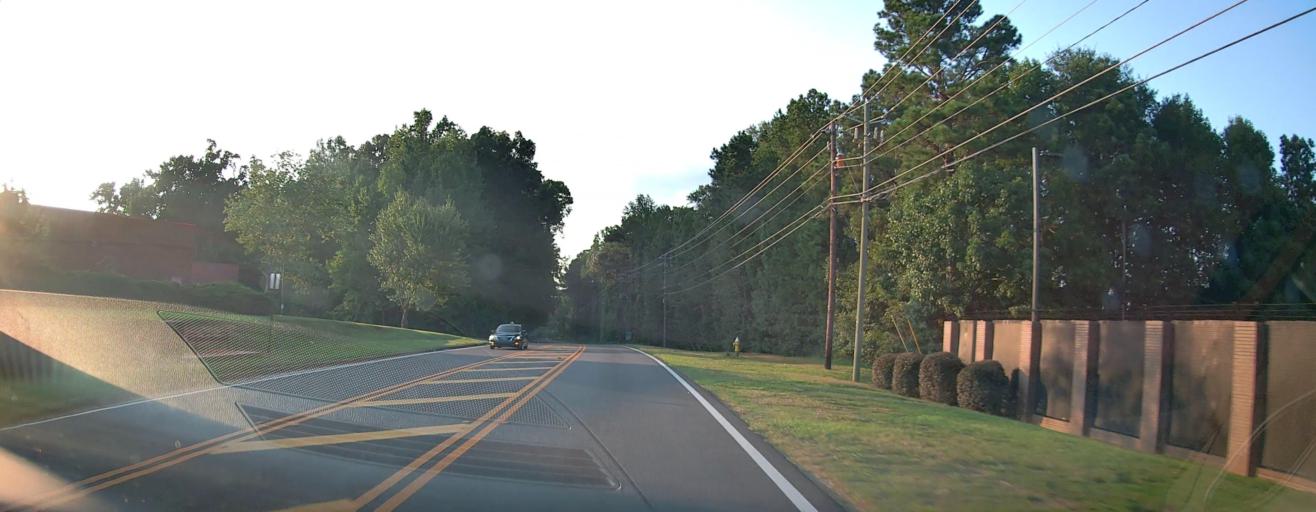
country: US
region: Georgia
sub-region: Bibb County
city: Macon
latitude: 32.9002
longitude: -83.7035
